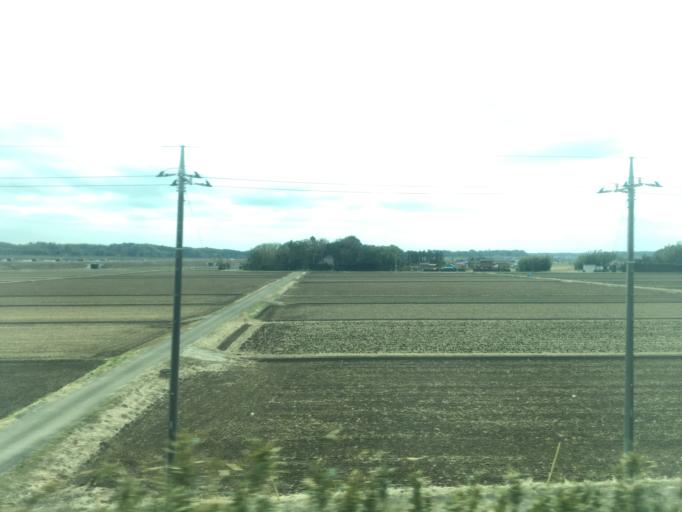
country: JP
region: Chiba
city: Narita
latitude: 35.8039
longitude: 140.2837
